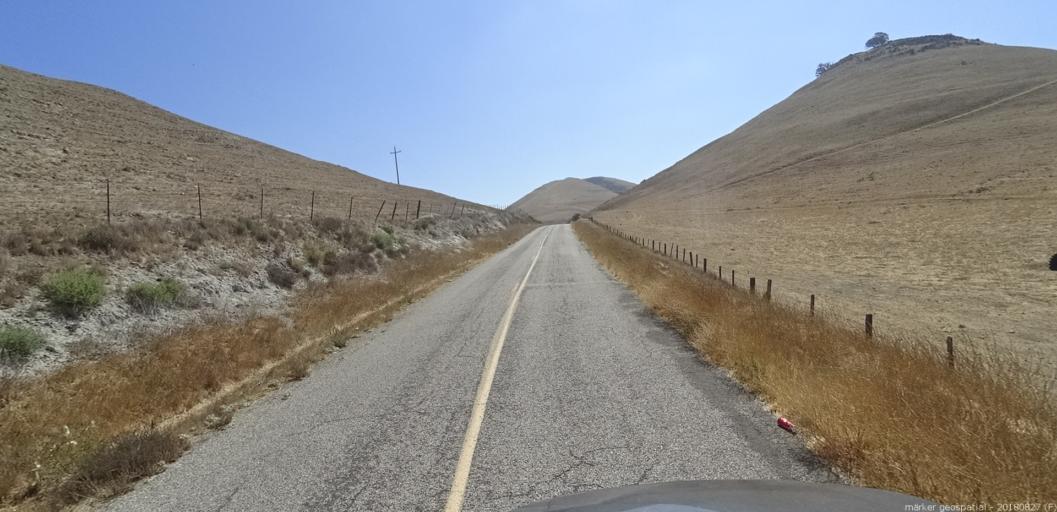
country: US
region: California
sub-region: Monterey County
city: King City
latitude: 36.2497
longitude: -121.0108
